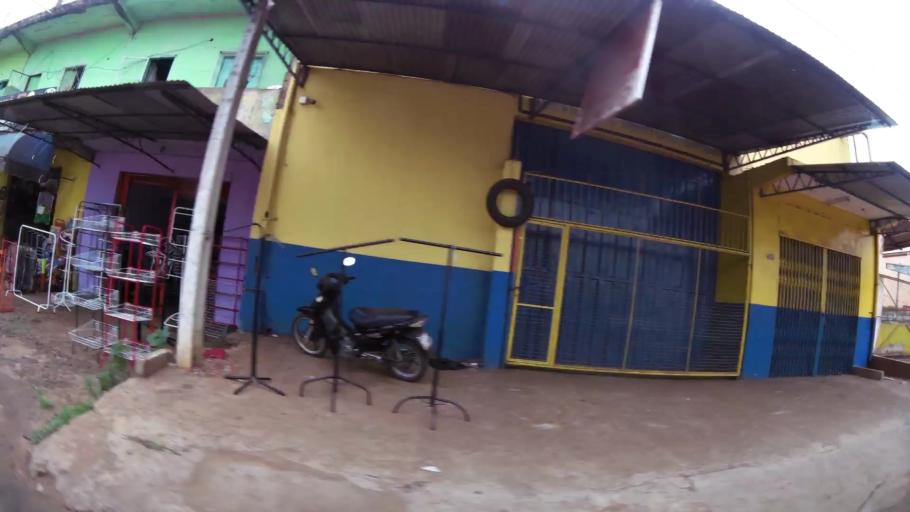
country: PY
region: Alto Parana
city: Presidente Franco
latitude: -25.5444
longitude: -54.6090
